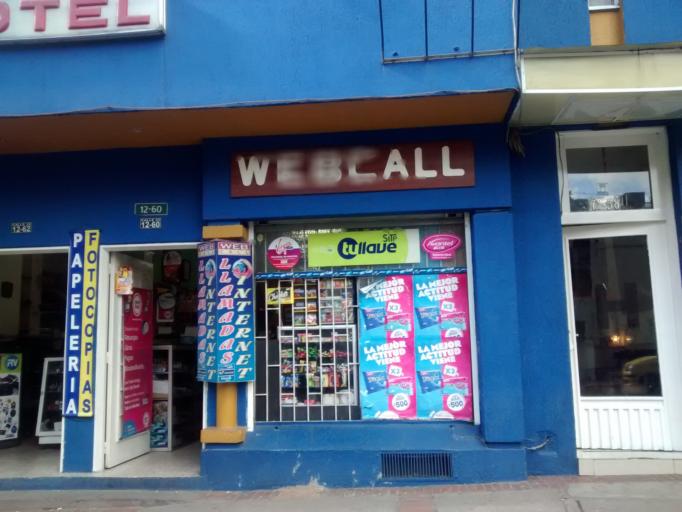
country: CO
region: Bogota D.C.
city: Bogota
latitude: 4.6098
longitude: -74.0734
